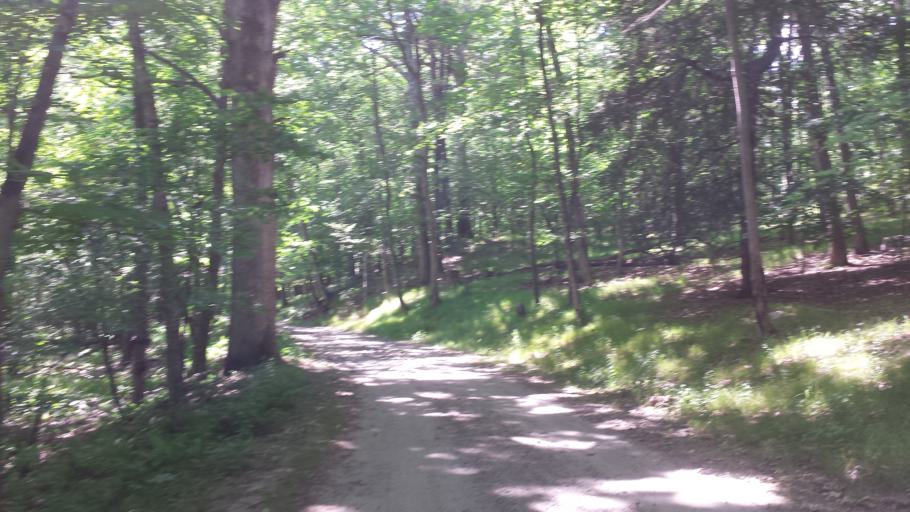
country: US
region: Connecticut
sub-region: Fairfield County
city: Ridgefield
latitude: 41.3091
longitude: -73.5539
